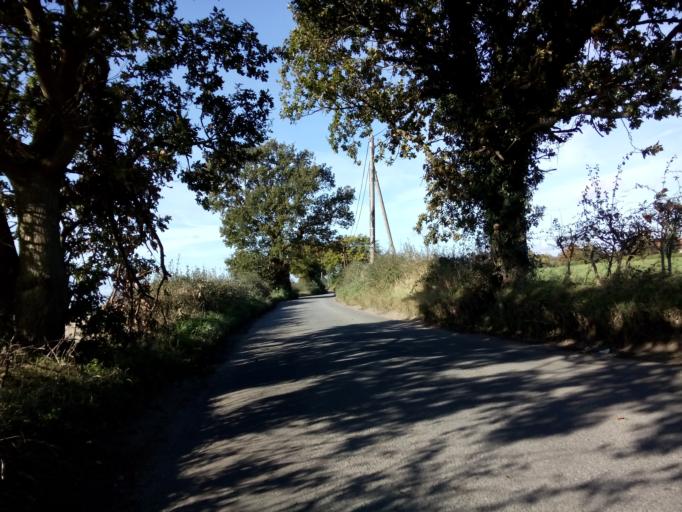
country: GB
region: England
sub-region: Suffolk
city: Bramford
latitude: 52.0256
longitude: 1.1012
